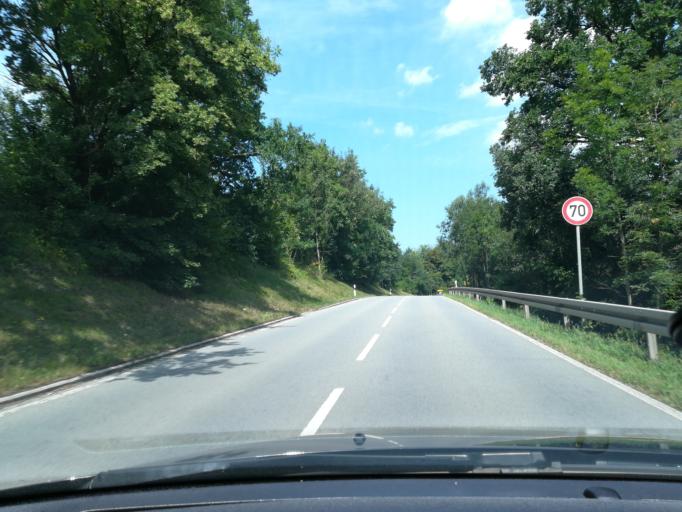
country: DE
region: Bavaria
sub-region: Upper Bavaria
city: Grafing bei Munchen
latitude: 48.0394
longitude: 11.9434
